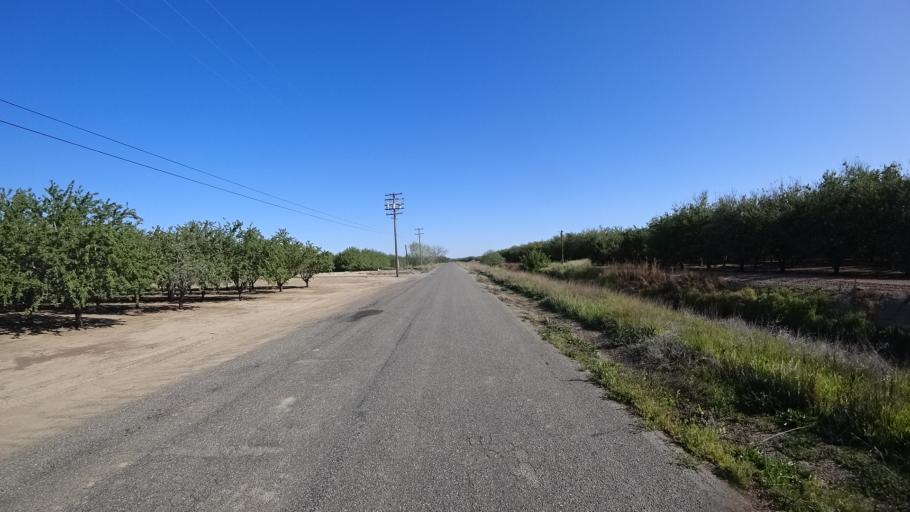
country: US
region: California
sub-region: Glenn County
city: Hamilton City
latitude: 39.7015
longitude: -122.0548
